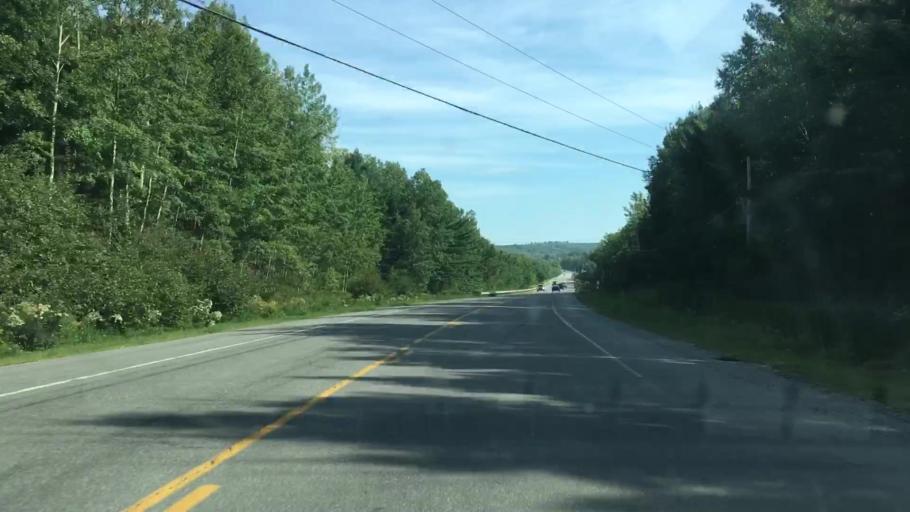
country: US
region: Maine
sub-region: Penobscot County
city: Lincoln
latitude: 45.3682
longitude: -68.5540
